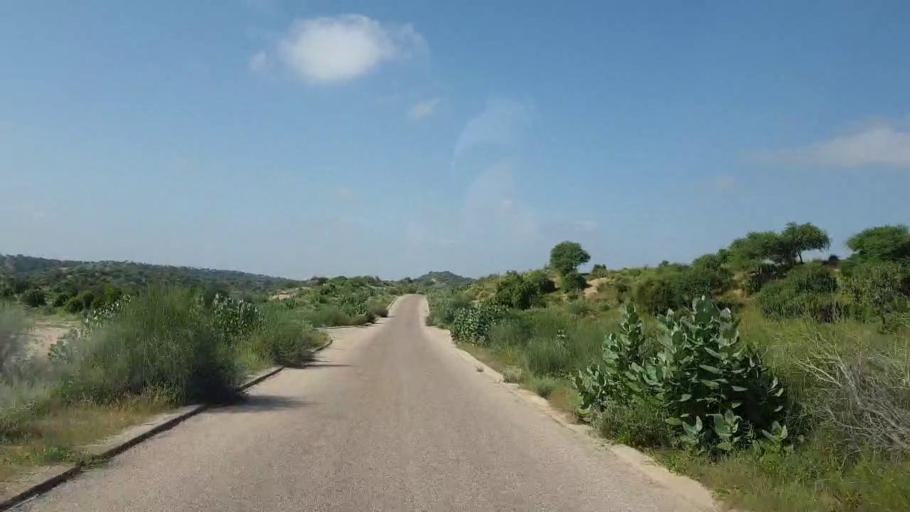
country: PK
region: Sindh
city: Mithi
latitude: 24.5538
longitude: 69.8921
